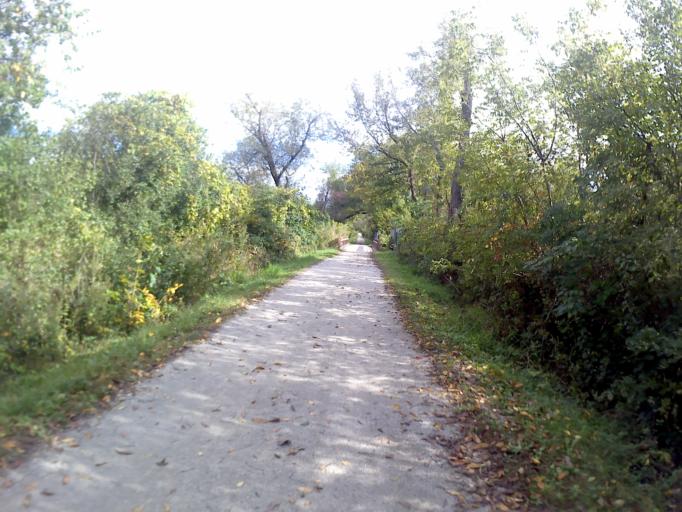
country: US
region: Illinois
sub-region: DuPage County
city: Winfield
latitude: 41.8909
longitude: -88.1568
